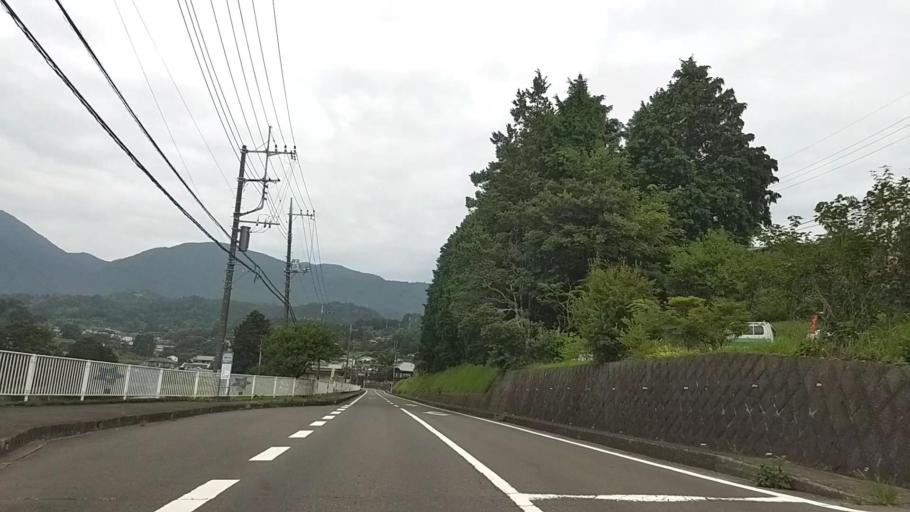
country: JP
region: Kanagawa
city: Odawara
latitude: 35.3300
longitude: 139.0839
